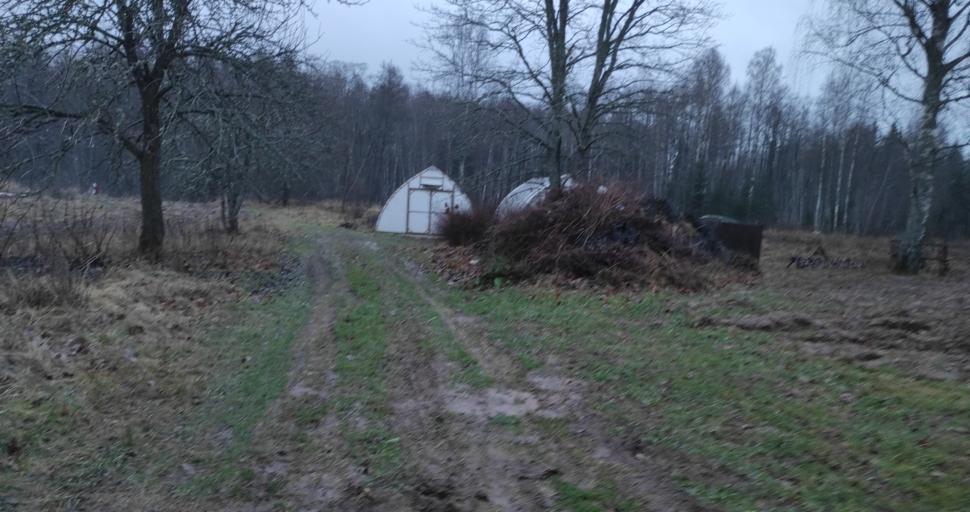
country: LV
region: Skrunda
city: Skrunda
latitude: 56.8530
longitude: 22.2567
